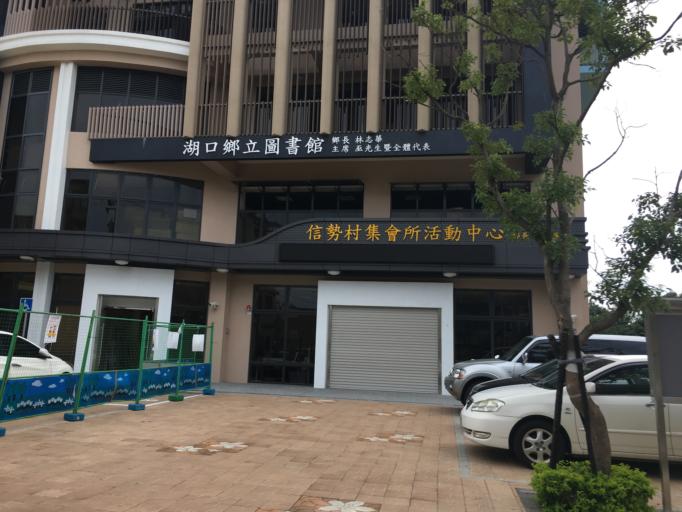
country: TW
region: Taiwan
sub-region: Hsinchu
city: Zhubei
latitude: 24.9018
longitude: 121.0380
